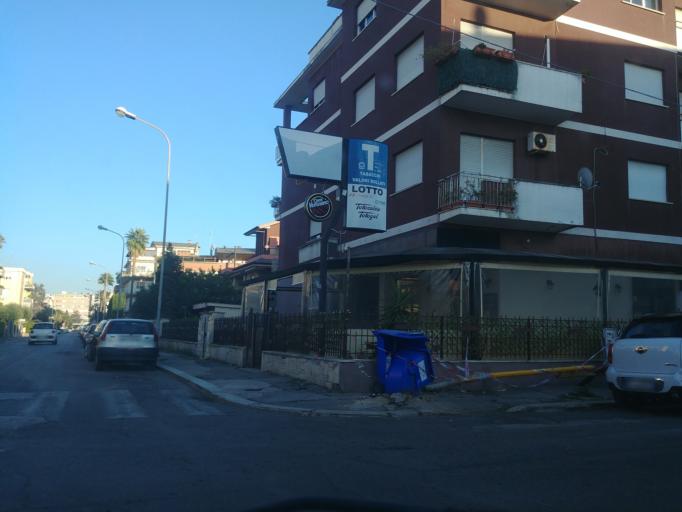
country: IT
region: Latium
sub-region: Provincia di Latina
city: Latina
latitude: 41.4605
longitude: 12.9027
